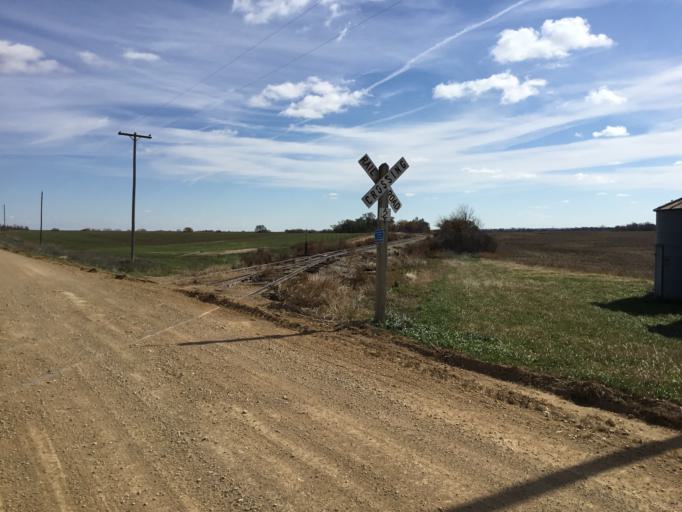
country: US
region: Kansas
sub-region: Lincoln County
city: Lincoln
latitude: 39.0601
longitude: -98.2435
